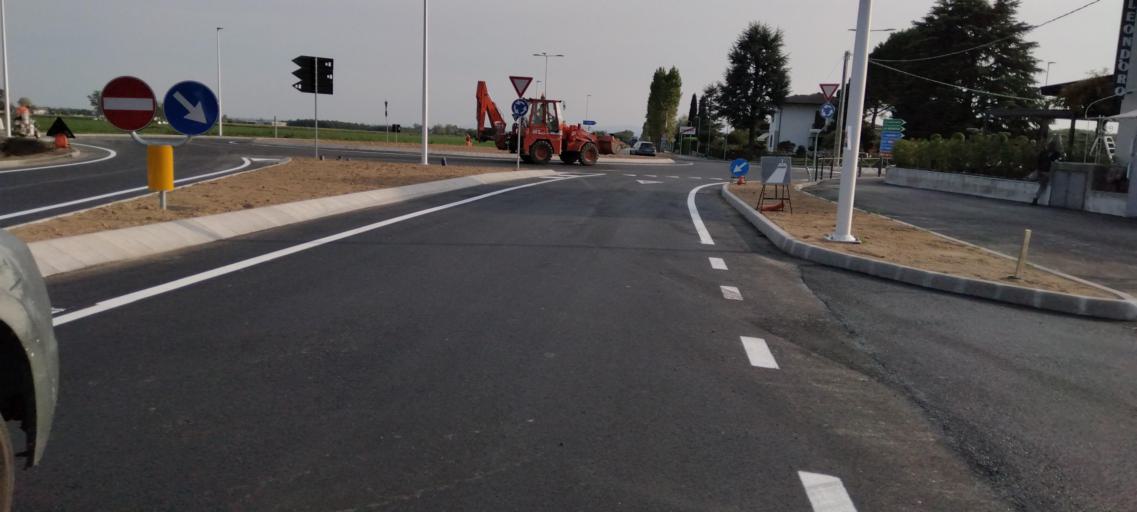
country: IT
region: Veneto
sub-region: Provincia di Vicenza
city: Thiene
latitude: 45.6849
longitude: 11.4845
